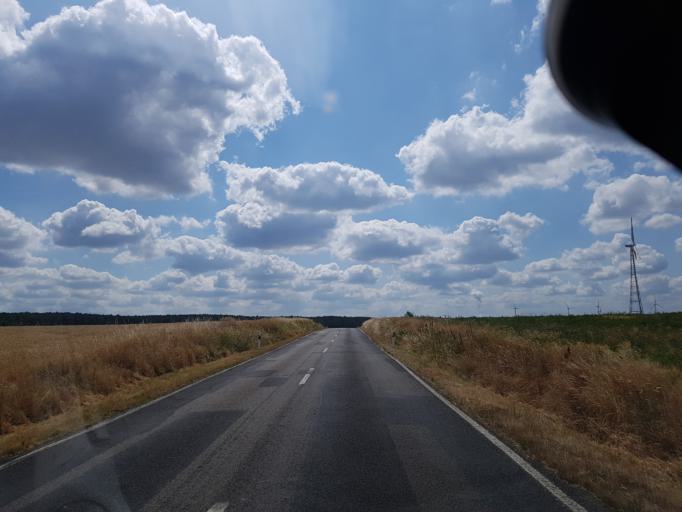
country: DE
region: Brandenburg
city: Drebkau
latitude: 51.6818
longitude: 14.2770
